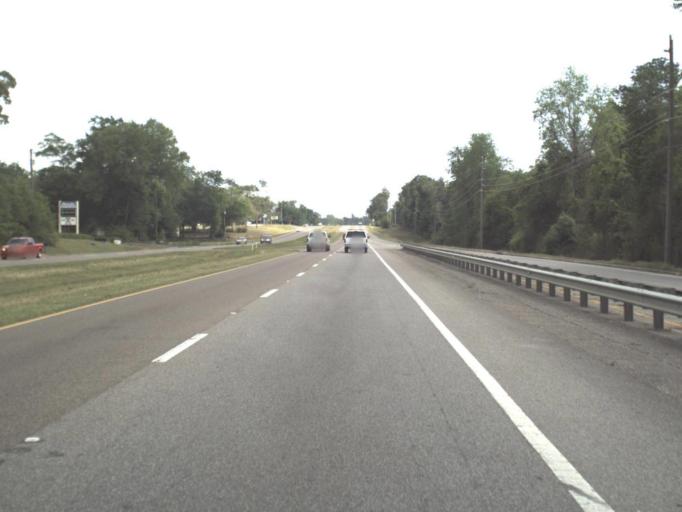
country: US
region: Florida
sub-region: Escambia County
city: Gonzalez
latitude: 30.5865
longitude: -87.3040
